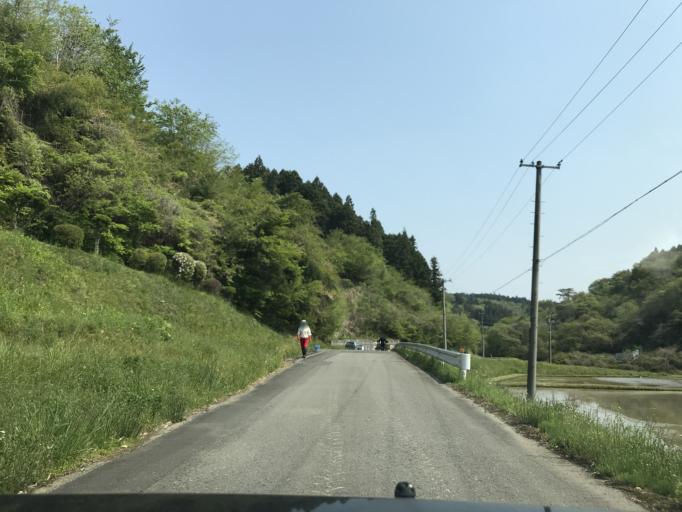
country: JP
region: Iwate
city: Ichinoseki
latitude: 38.8935
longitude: 141.1023
